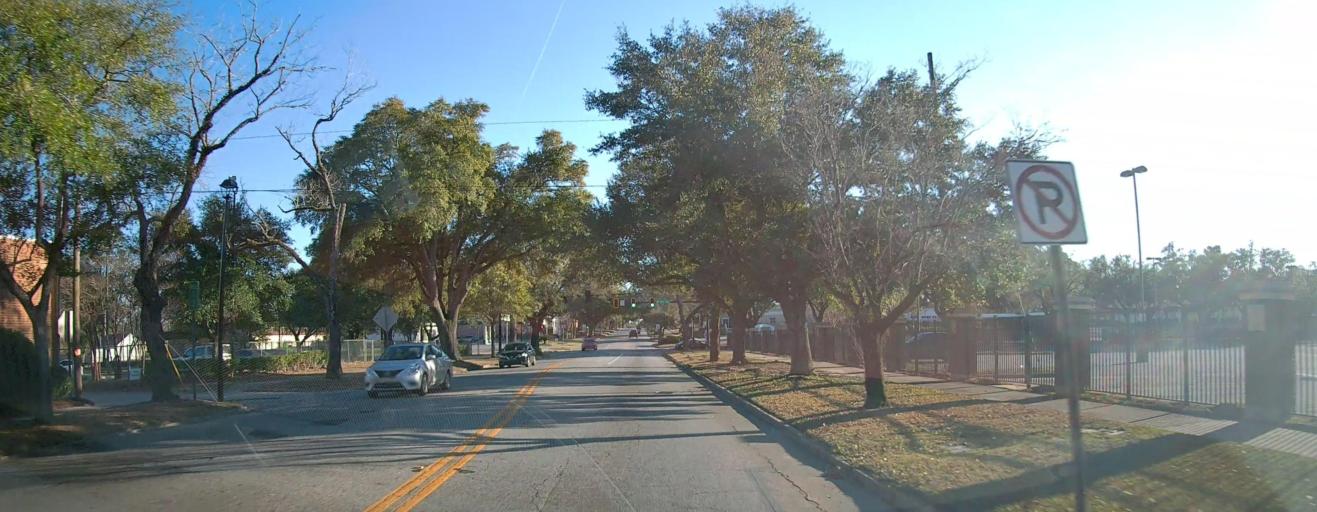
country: US
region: Georgia
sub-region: Dougherty County
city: Albany
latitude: 31.5898
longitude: -84.1561
